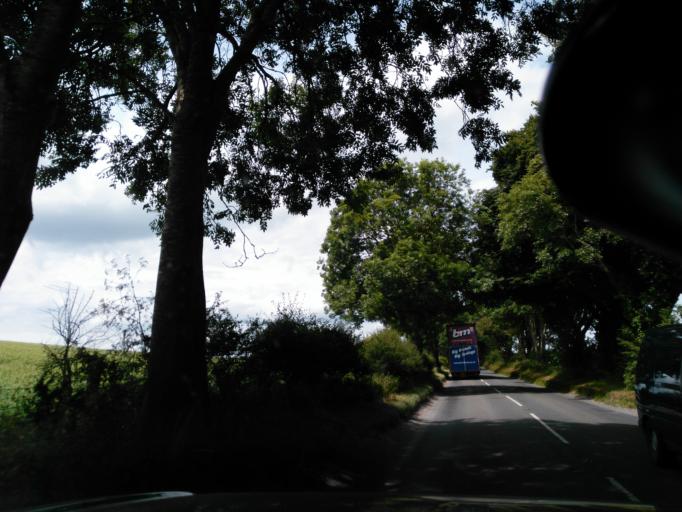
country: GB
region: England
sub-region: Wiltshire
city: Woodford
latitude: 51.1091
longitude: -1.8453
